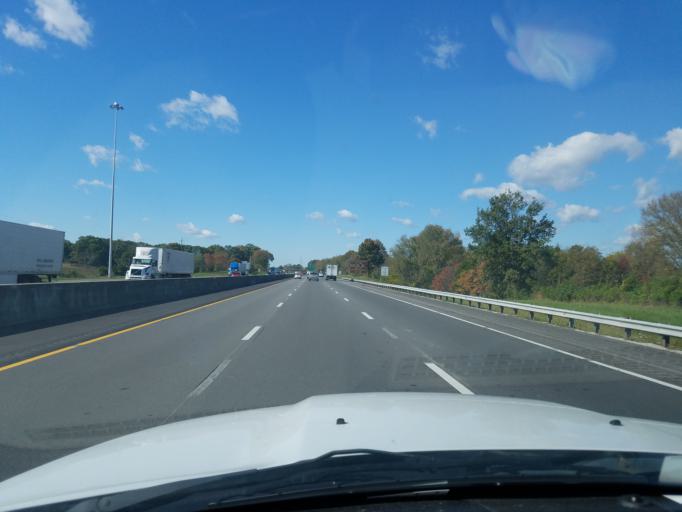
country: US
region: Kentucky
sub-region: Warren County
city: Bowling Green
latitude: 37.0109
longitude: -86.3431
